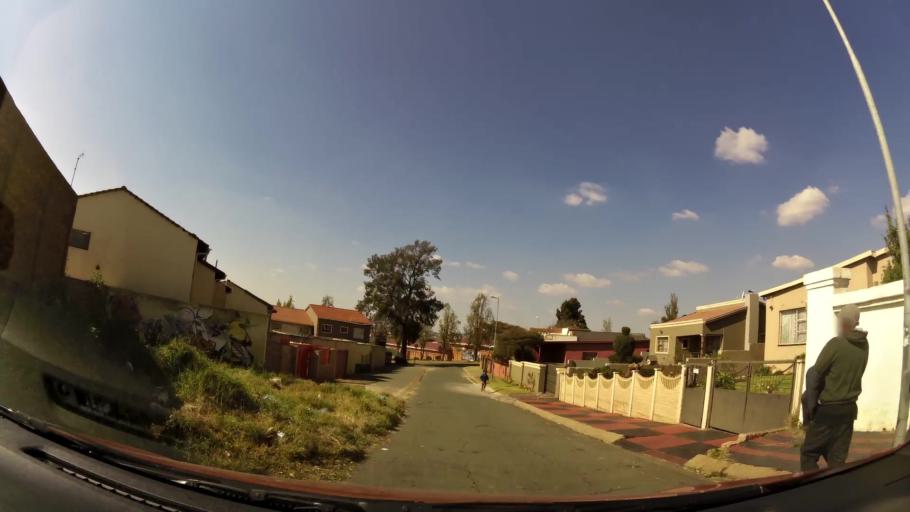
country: ZA
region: Gauteng
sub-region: City of Johannesburg Metropolitan Municipality
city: Soweto
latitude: -26.2381
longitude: 27.9053
